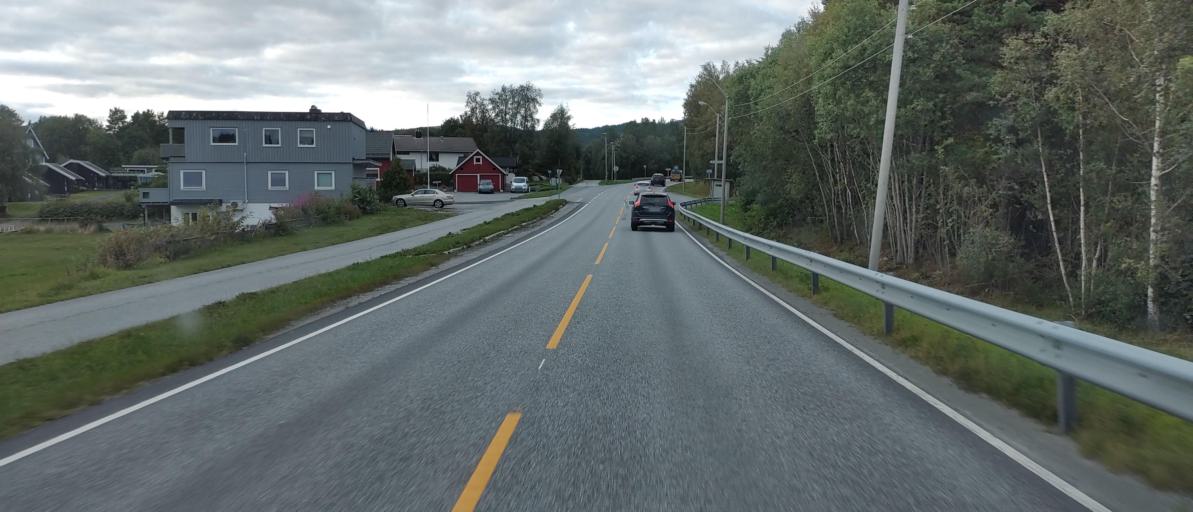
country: NO
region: More og Romsdal
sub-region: Molde
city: Hjelset
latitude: 62.7171
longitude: 7.4279
